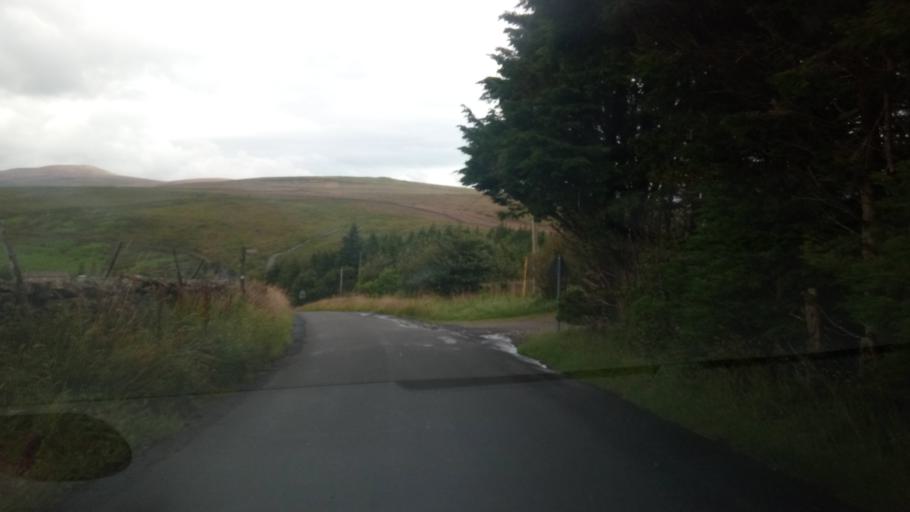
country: GB
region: England
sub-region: Cumbria
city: Kirkby Stephen
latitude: 54.3214
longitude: -2.3285
